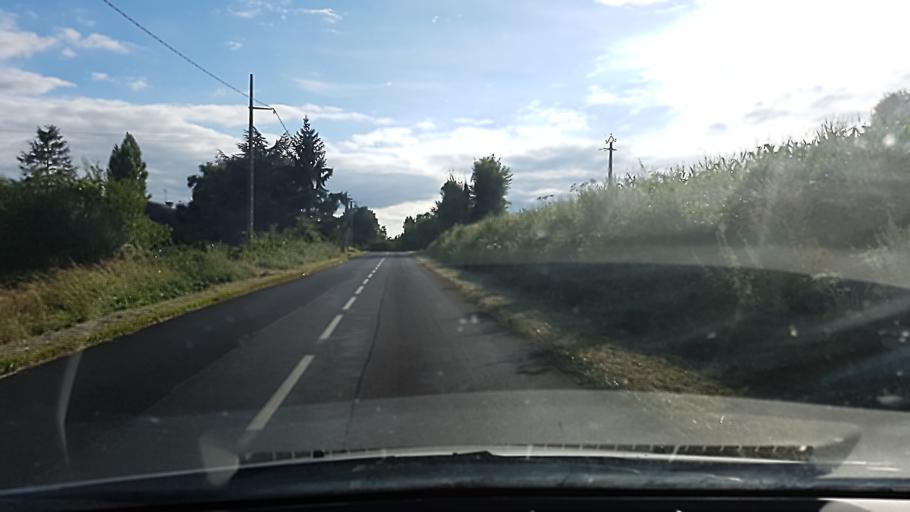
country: FR
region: Pays de la Loire
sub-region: Departement de Maine-et-Loire
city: Maze
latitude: 47.4975
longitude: -0.2647
